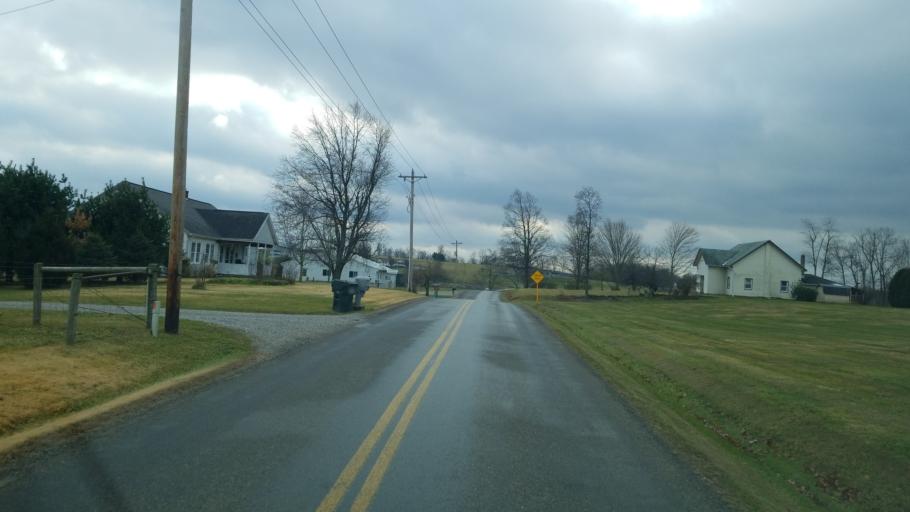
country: US
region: Ohio
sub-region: Holmes County
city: Millersburg
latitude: 40.5805
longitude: -81.9638
